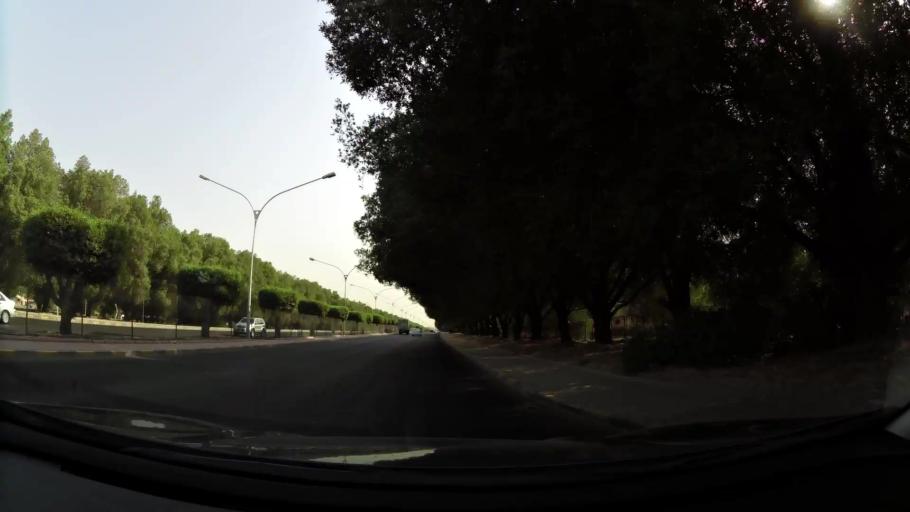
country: KW
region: Mubarak al Kabir
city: Sabah as Salim
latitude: 29.2792
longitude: 48.0626
